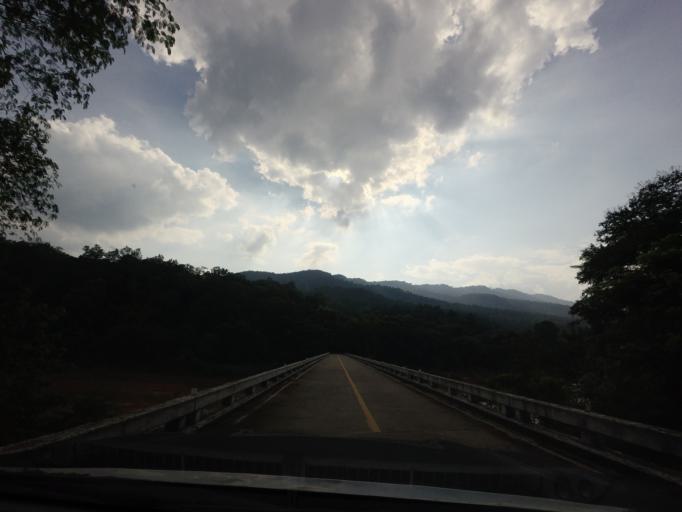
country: TH
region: Nan
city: Na Noi
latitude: 18.3311
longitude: 100.8924
